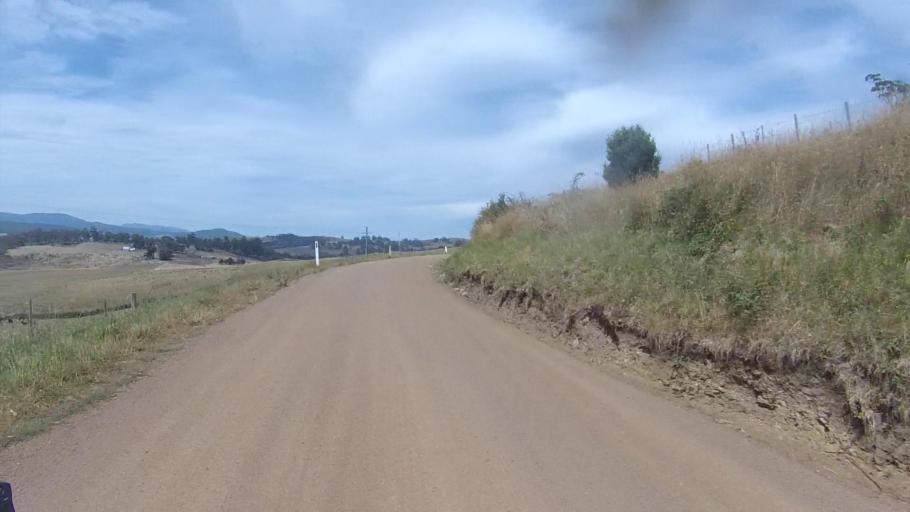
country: AU
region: Tasmania
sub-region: Sorell
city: Sorell
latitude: -42.7950
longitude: 147.8386
